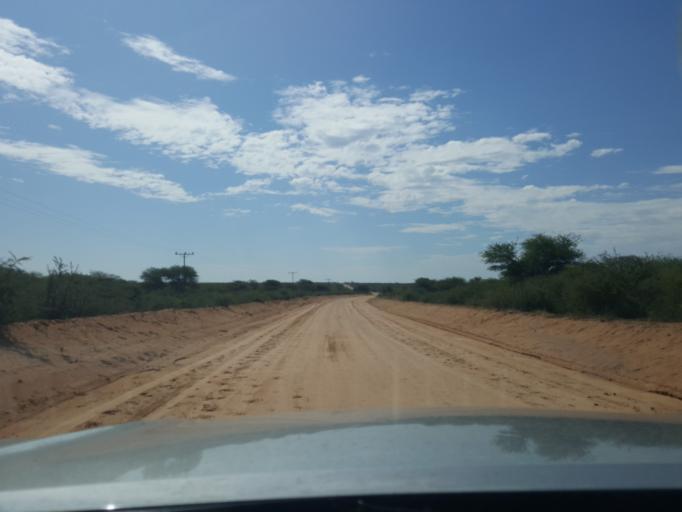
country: BW
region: Kweneng
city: Khudumelapye
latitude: -23.8855
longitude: 24.9117
